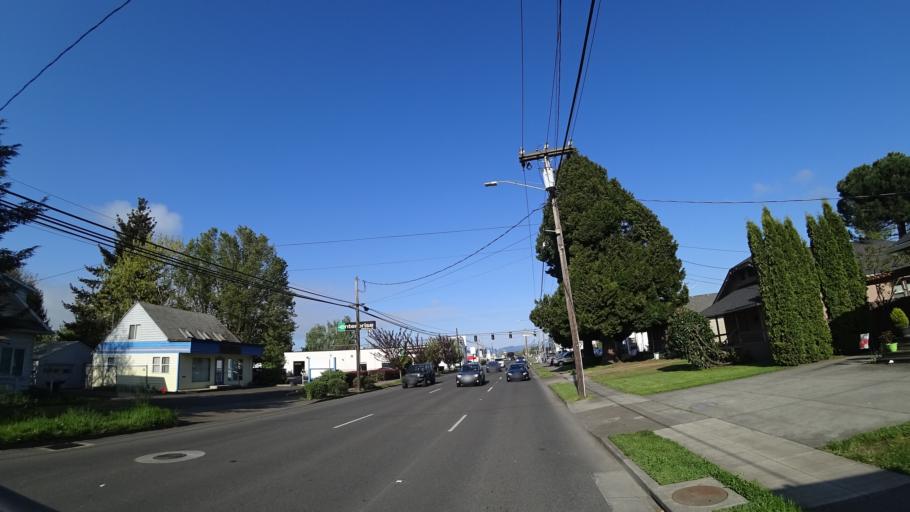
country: US
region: Oregon
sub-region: Washington County
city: Hillsboro
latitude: 45.5189
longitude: -122.9948
